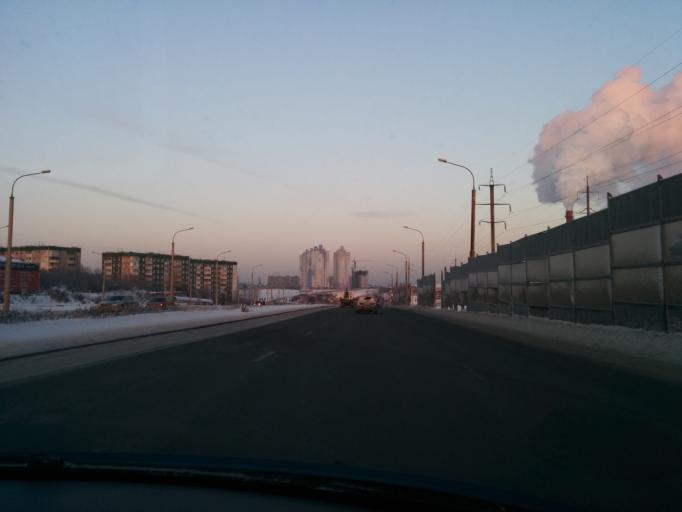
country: RU
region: Perm
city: Perm
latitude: 57.9967
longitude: 56.3084
